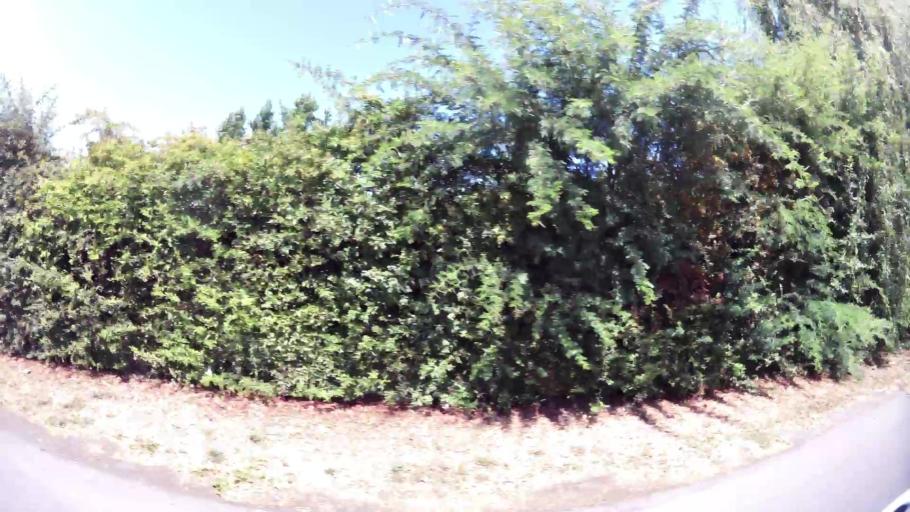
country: CL
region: Maule
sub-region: Provincia de Curico
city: Curico
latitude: -34.9935
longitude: -71.2081
